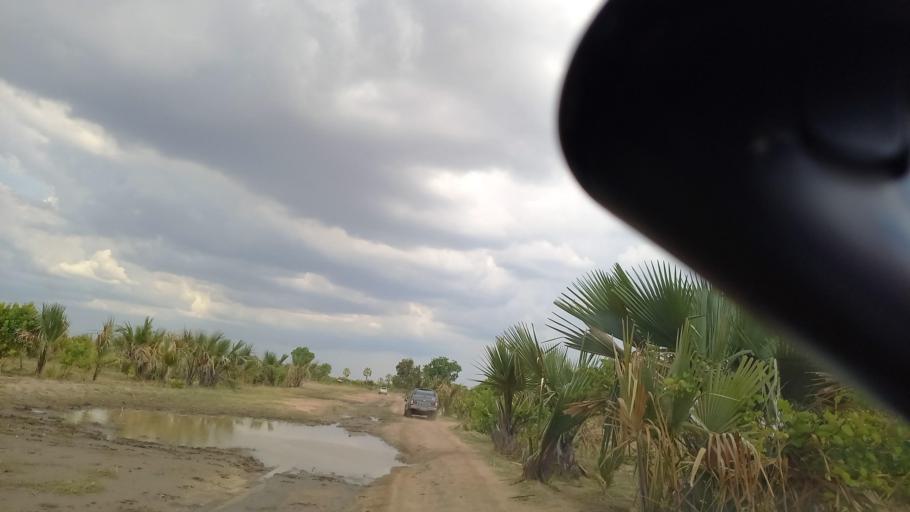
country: ZM
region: Lusaka
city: Kafue
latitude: -15.8354
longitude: 28.0766
